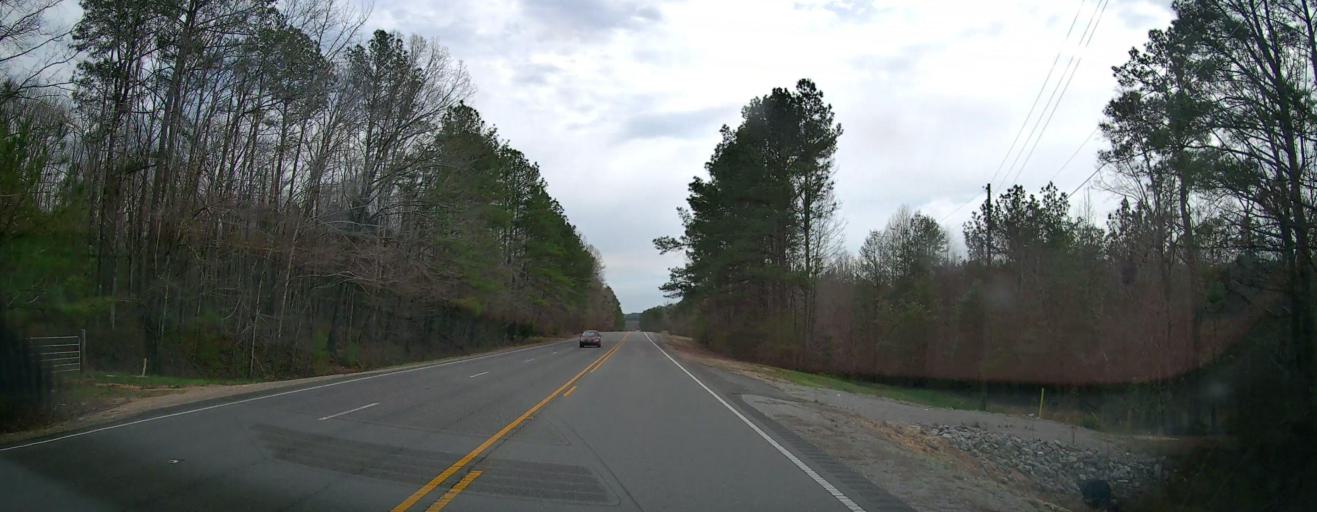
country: US
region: Alabama
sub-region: Marion County
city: Guin
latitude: 34.0181
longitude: -87.9378
